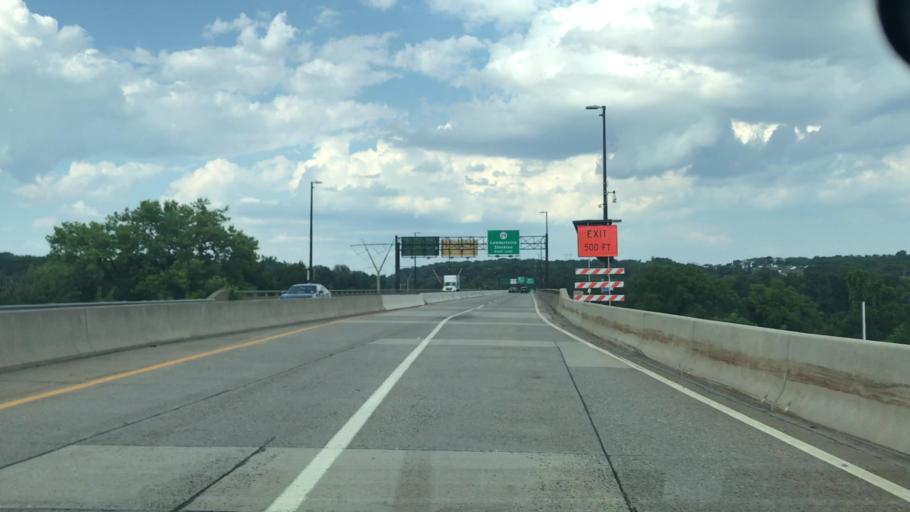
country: US
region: Pennsylvania
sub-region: Bucks County
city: New Hope
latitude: 40.3783
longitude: -74.9583
